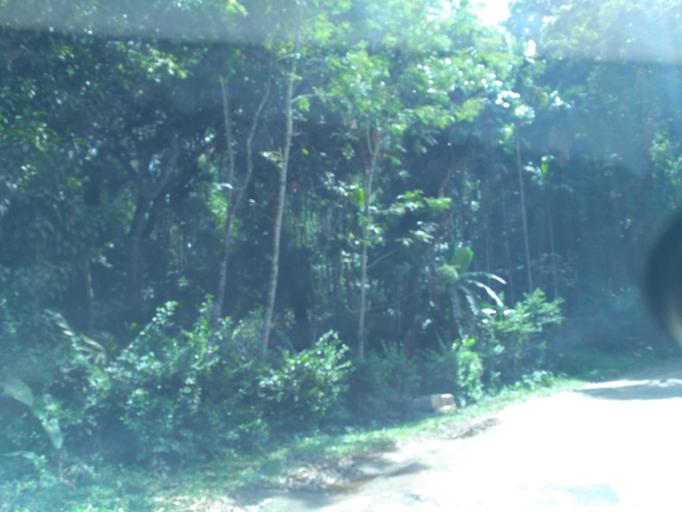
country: IN
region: Karnataka
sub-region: Kodagu
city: Madikeri
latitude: 12.3890
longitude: 75.7147
